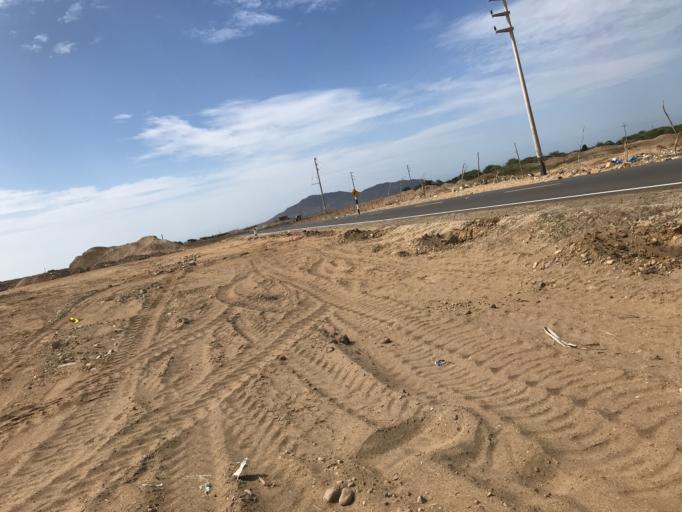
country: PE
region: Lambayeque
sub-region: Provincia de Chiclayo
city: Eten
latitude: -6.9002
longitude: -79.8443
